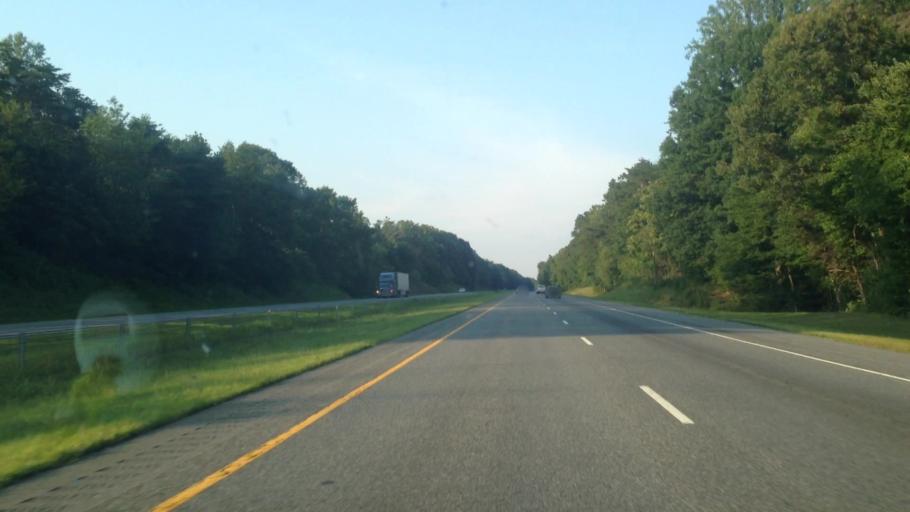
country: US
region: North Carolina
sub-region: Rockingham County
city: Reidsville
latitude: 36.4119
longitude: -79.5897
